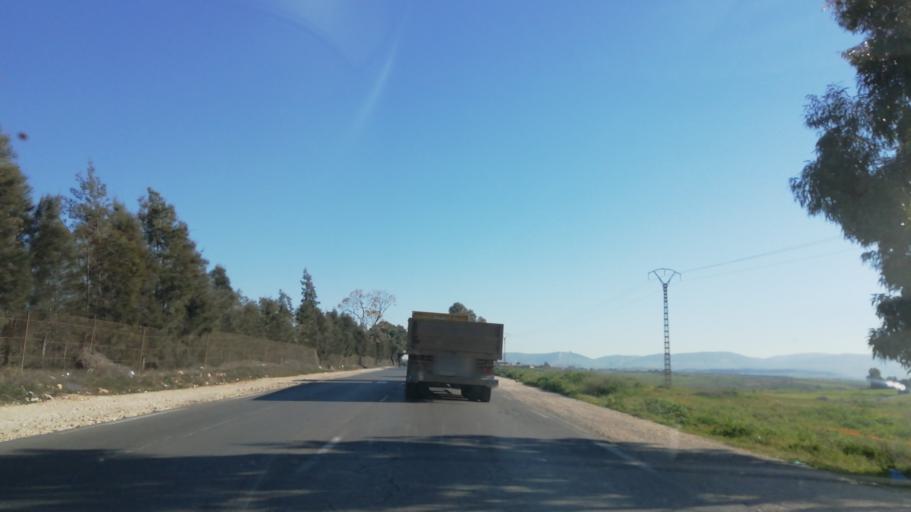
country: DZ
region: Relizane
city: Zemoura
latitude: 35.7529
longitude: 0.6839
